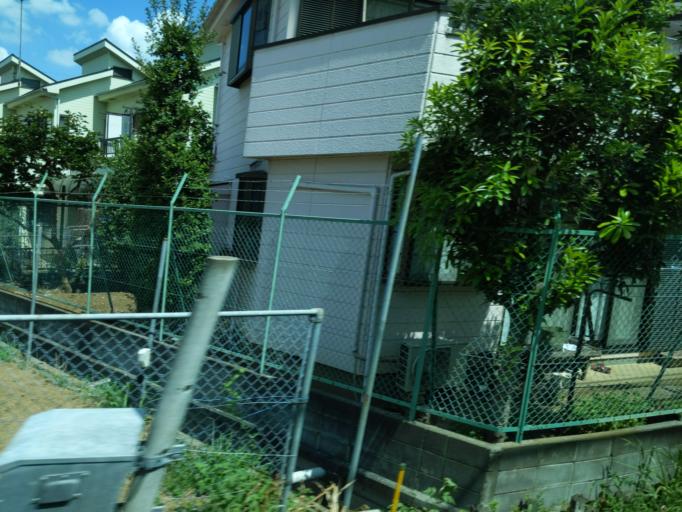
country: JP
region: Tokyo
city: Chofugaoka
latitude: 35.6292
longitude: 139.5548
